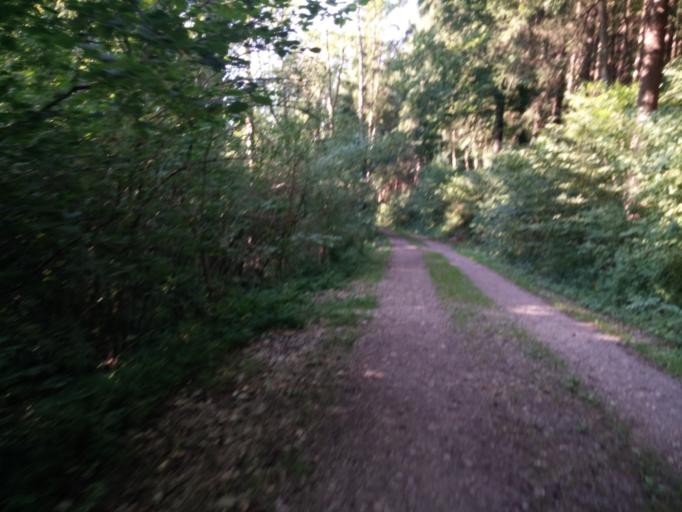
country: DE
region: Bavaria
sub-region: Swabia
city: Lautrach
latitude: 47.8928
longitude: 10.1223
